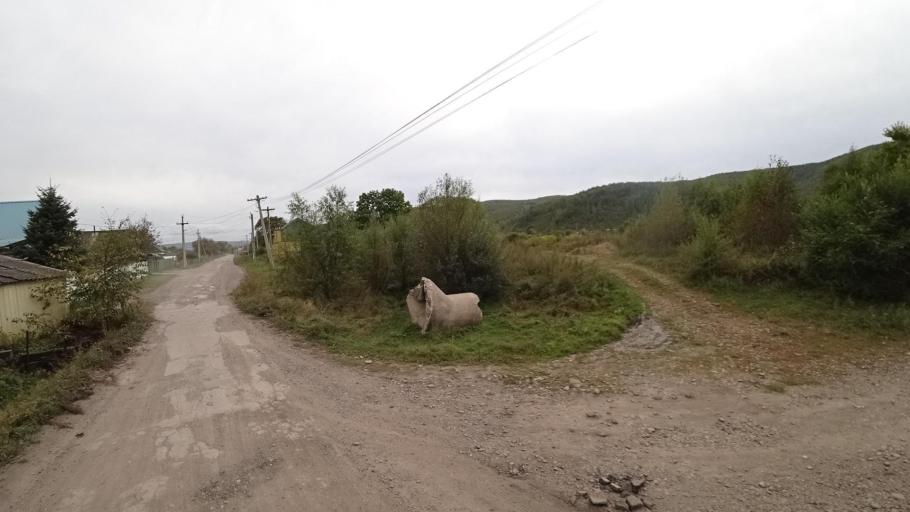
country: RU
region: Jewish Autonomous Oblast
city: Khingansk
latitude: 49.0365
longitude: 131.0495
